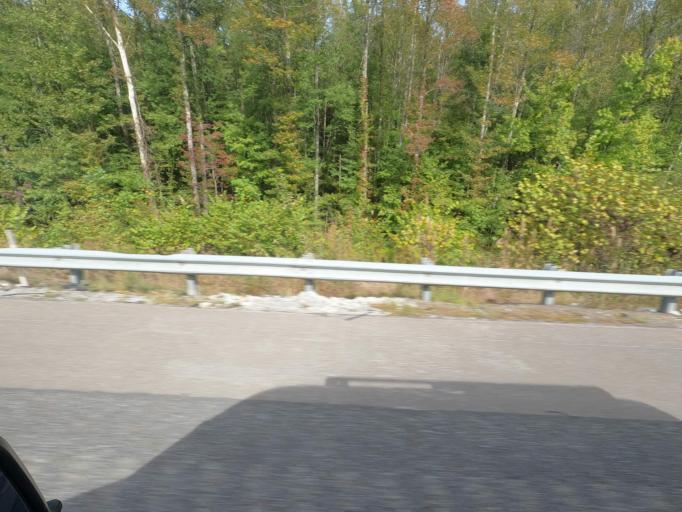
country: US
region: Tennessee
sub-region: Decatur County
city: Parsons
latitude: 35.8153
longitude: -88.2149
